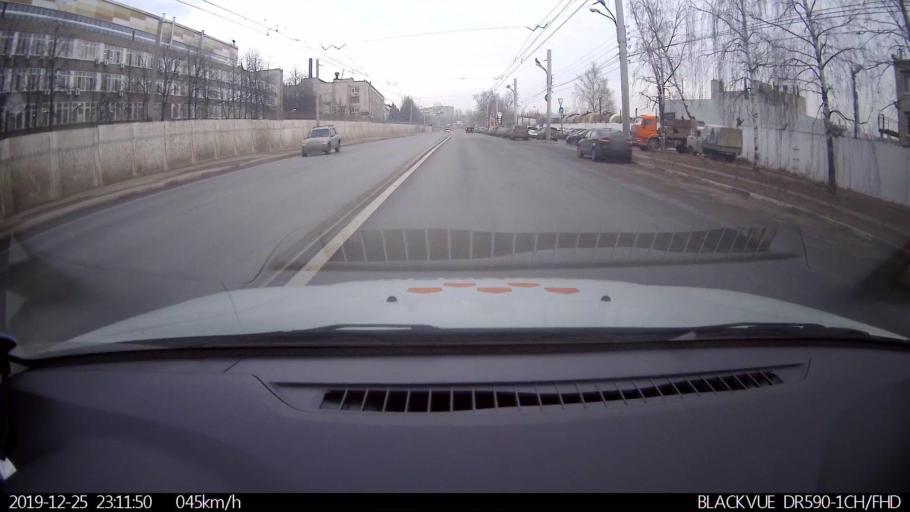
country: RU
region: Nizjnij Novgorod
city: Nizhniy Novgorod
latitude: 56.3210
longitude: 43.9081
